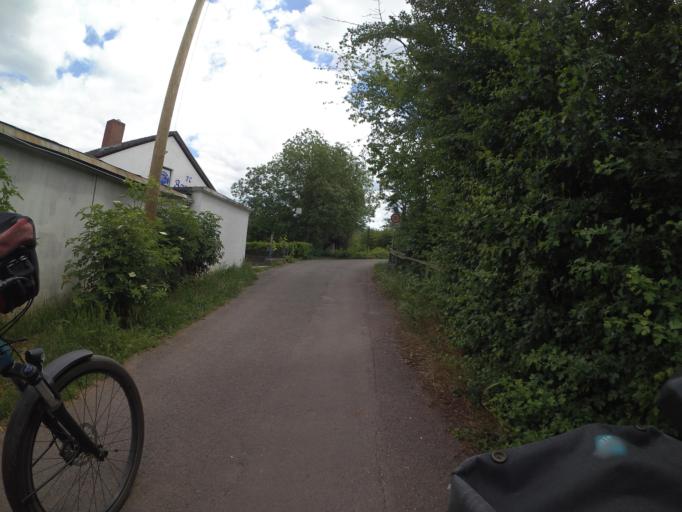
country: DE
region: Rheinland-Pfalz
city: Bad Munster am Stein-Ebernburg
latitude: 49.8130
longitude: 7.8342
